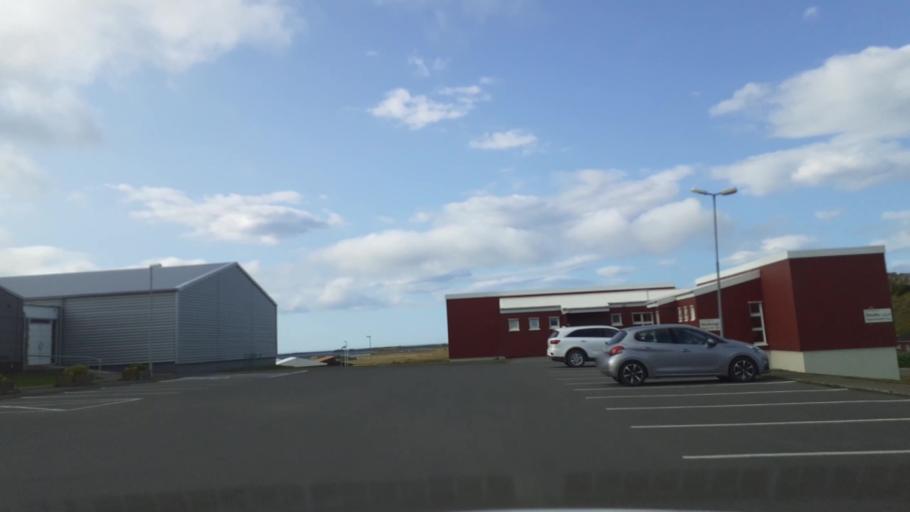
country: IS
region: East
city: Reydarfjoerdur
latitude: 64.6552
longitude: -14.2795
